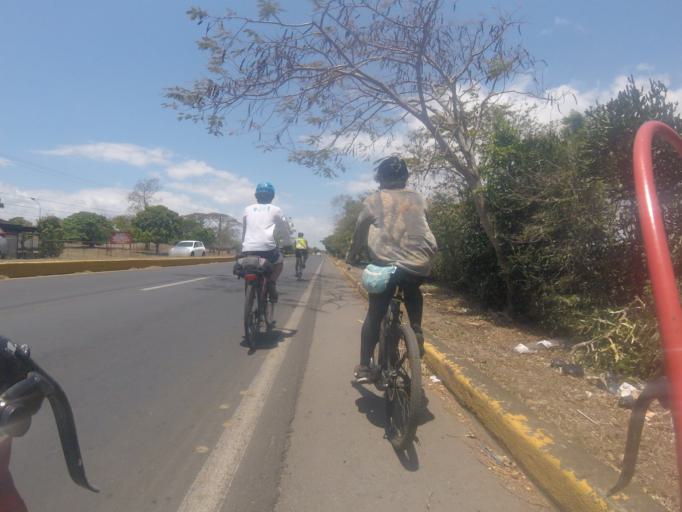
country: NI
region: Granada
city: Granada
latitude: 11.9503
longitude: -85.9851
